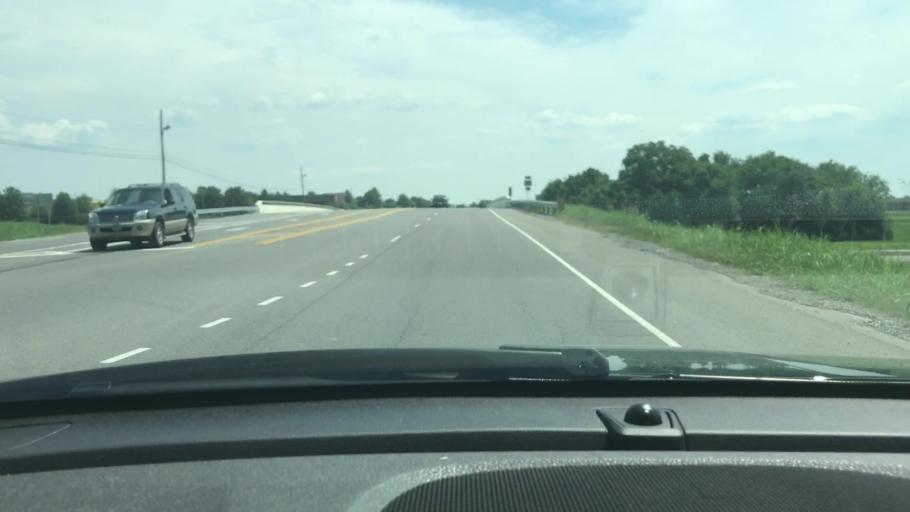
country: US
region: Tennessee
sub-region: Sumner County
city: Hendersonville
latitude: 36.3339
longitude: -86.5935
